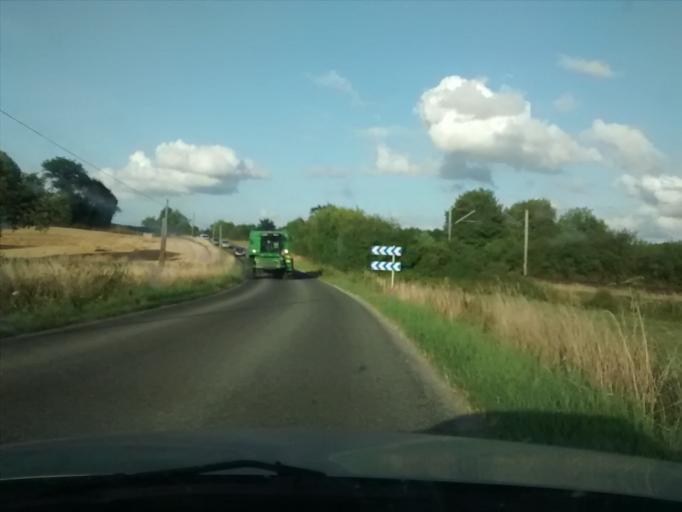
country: FR
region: Pays de la Loire
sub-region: Departement de la Mayenne
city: Montsurs
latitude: 48.1508
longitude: -0.5005
